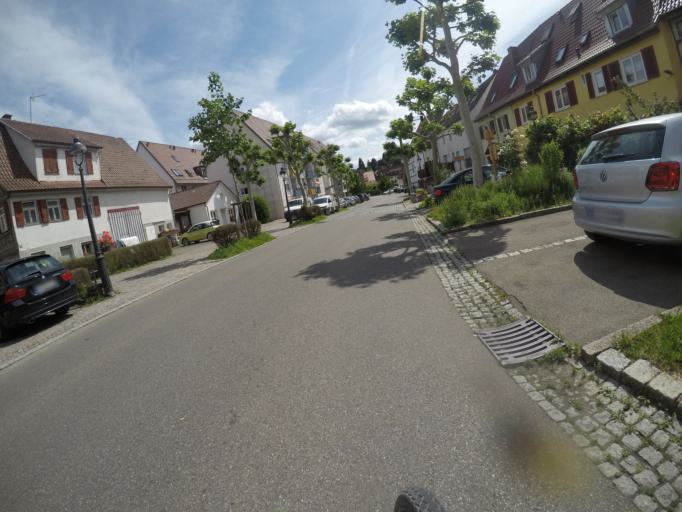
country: DE
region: Baden-Wuerttemberg
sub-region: Regierungsbezirk Stuttgart
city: Waldenbuch
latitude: 48.6372
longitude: 9.1332
